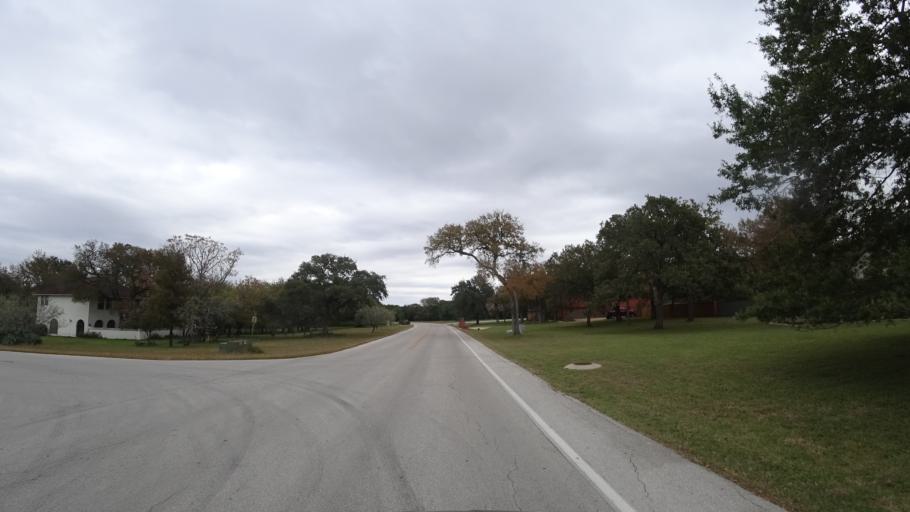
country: US
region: Texas
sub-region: Travis County
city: Shady Hollow
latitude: 30.1554
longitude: -97.8692
